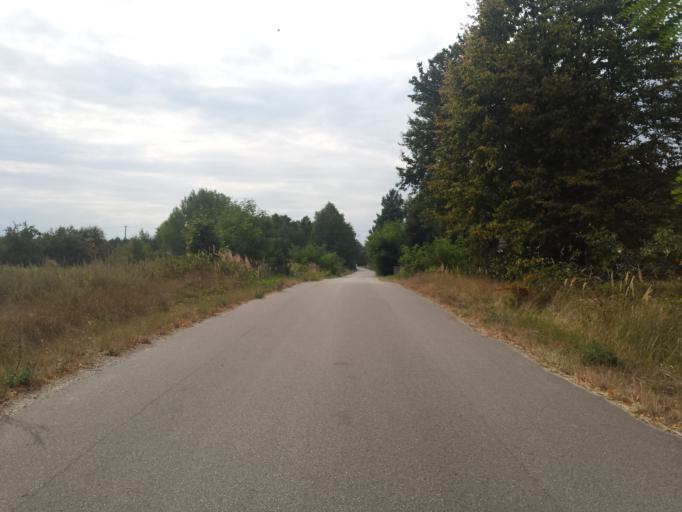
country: PL
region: Swietokrzyskie
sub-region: Powiat kielecki
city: Rakow
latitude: 50.6674
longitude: 21.1369
